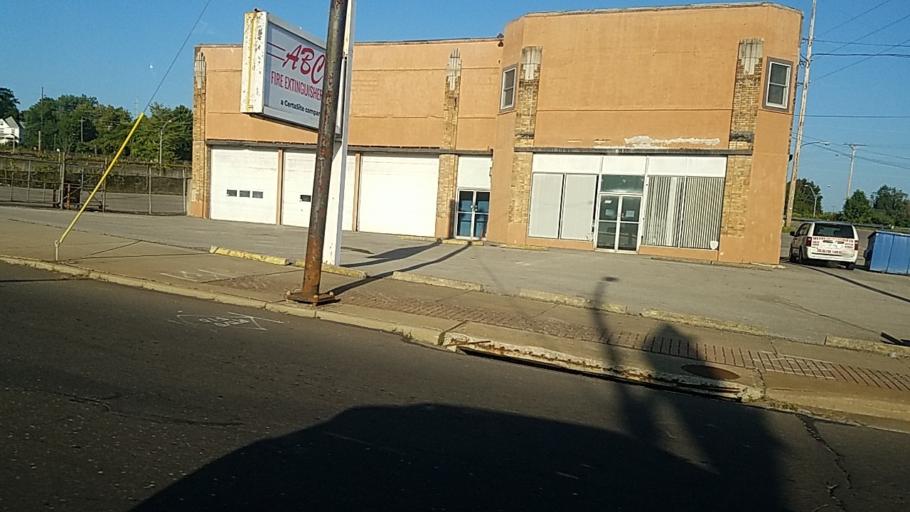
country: US
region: Ohio
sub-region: Mahoning County
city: Youngstown
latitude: 41.0932
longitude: -80.6546
